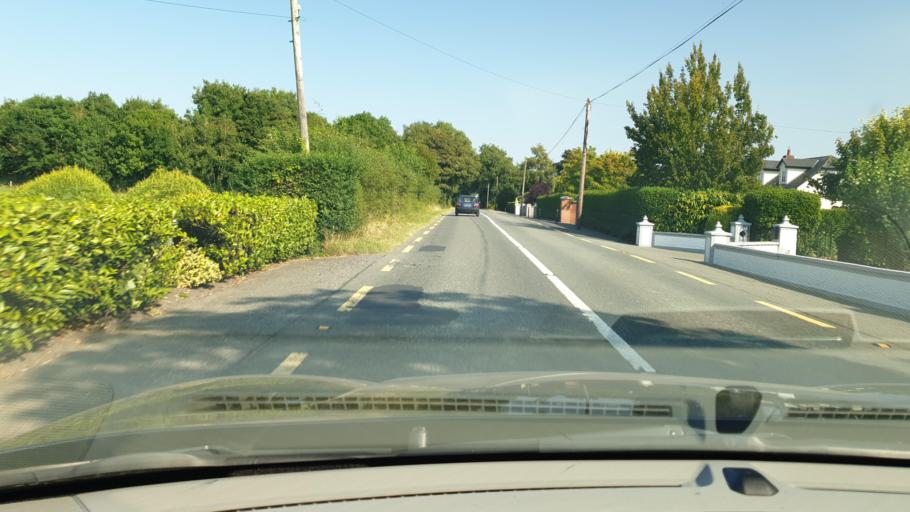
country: IE
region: Leinster
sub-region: An Mhi
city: Trim
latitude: 53.6328
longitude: -6.8059
